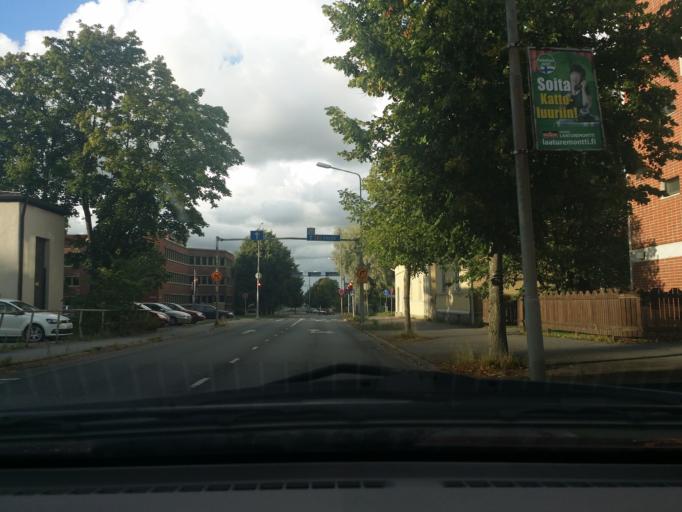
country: FI
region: Satakunta
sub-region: Pori
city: Pori
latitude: 61.4866
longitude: 21.8024
